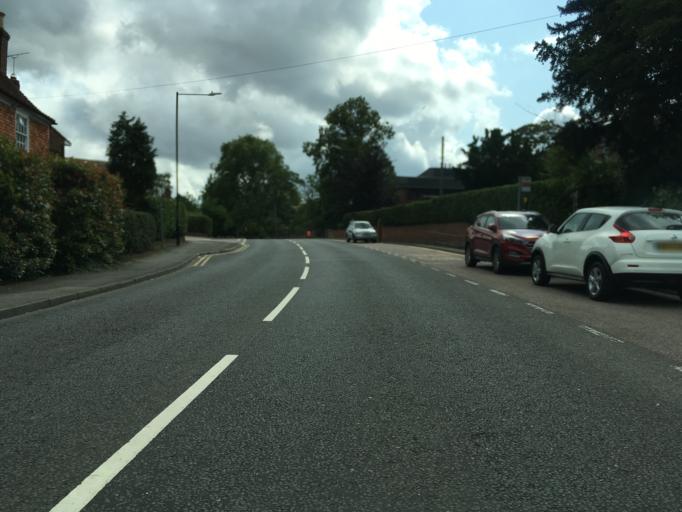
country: GB
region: England
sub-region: Kent
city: Tenterden
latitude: 51.0771
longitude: 0.6947
